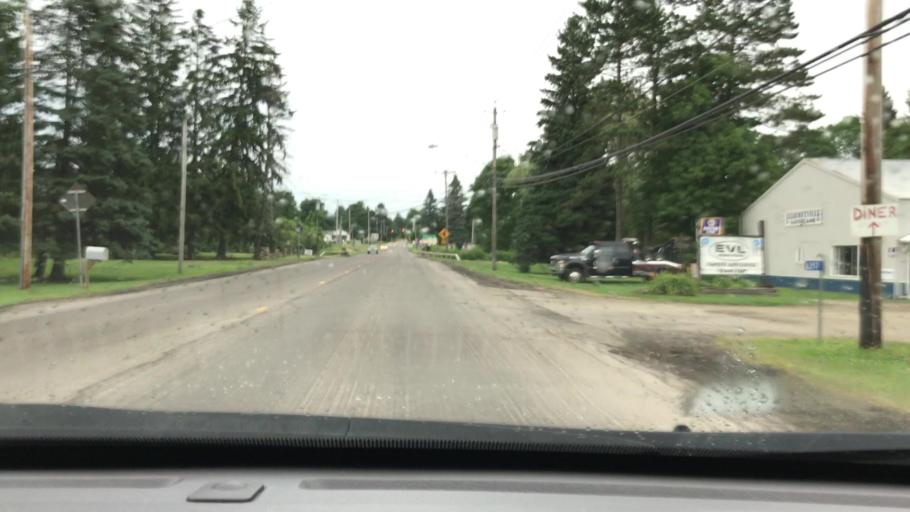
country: US
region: New York
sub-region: Cattaraugus County
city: Salamanca
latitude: 42.2835
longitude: -78.6620
